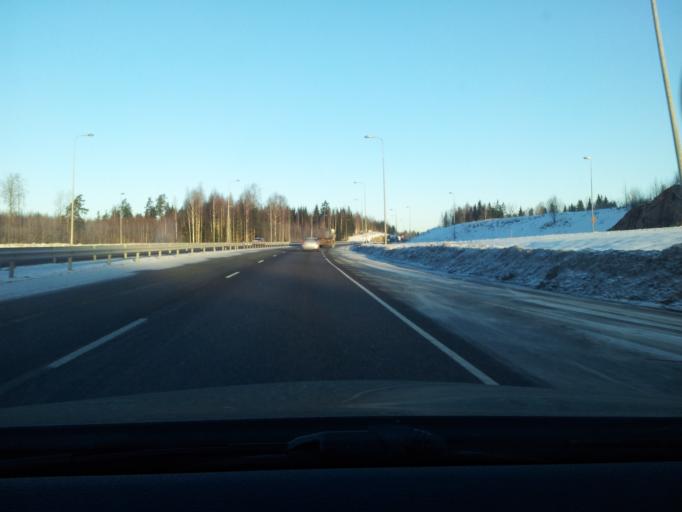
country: FI
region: Uusimaa
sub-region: Helsinki
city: Vihti
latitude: 60.3030
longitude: 24.3539
